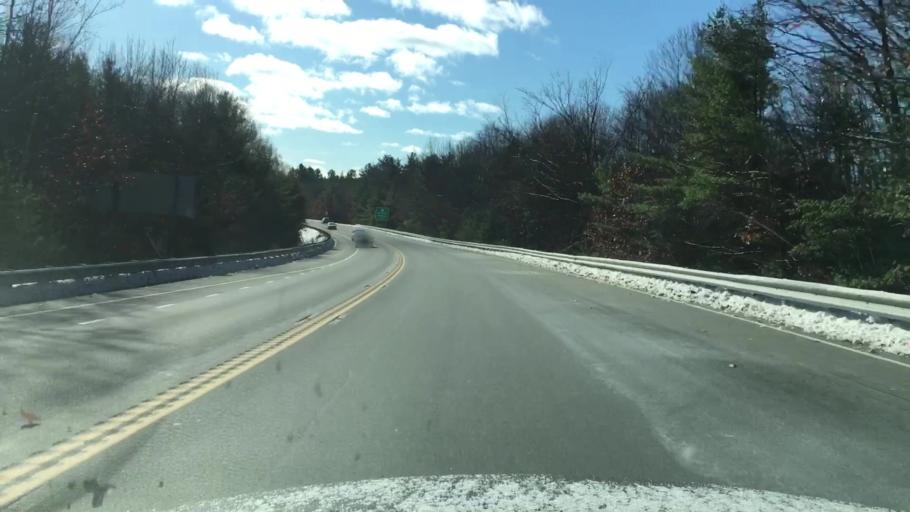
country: US
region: New Hampshire
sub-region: Hillsborough County
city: Milford
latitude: 42.8406
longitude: -71.6188
